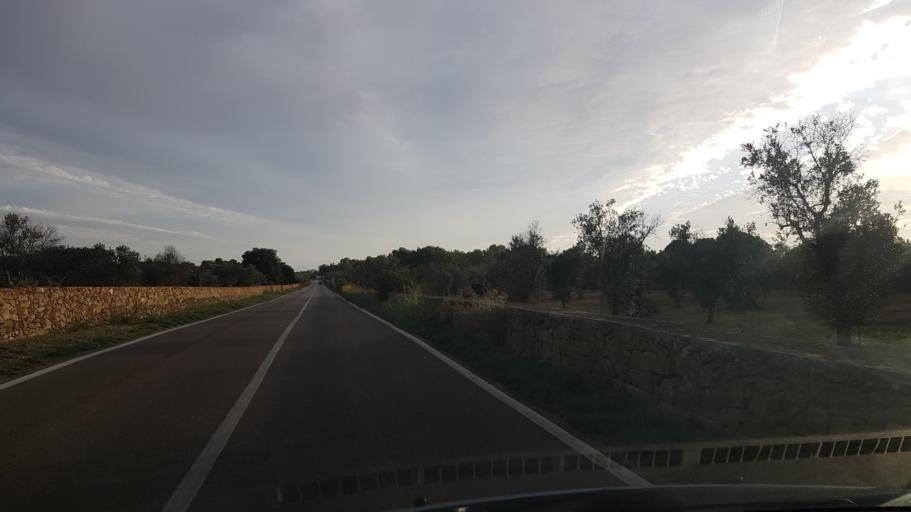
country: IT
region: Apulia
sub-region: Provincia di Brindisi
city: Torchiarolo
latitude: 40.4653
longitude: 18.1176
